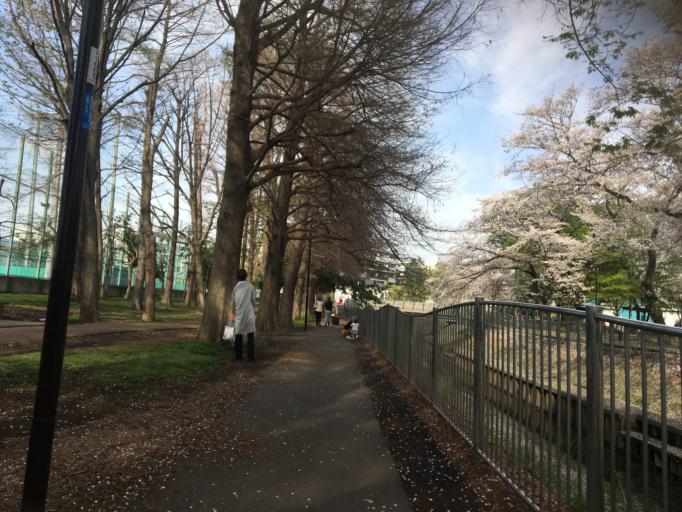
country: JP
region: Tokyo
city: Tokyo
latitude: 35.6949
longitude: 139.6315
